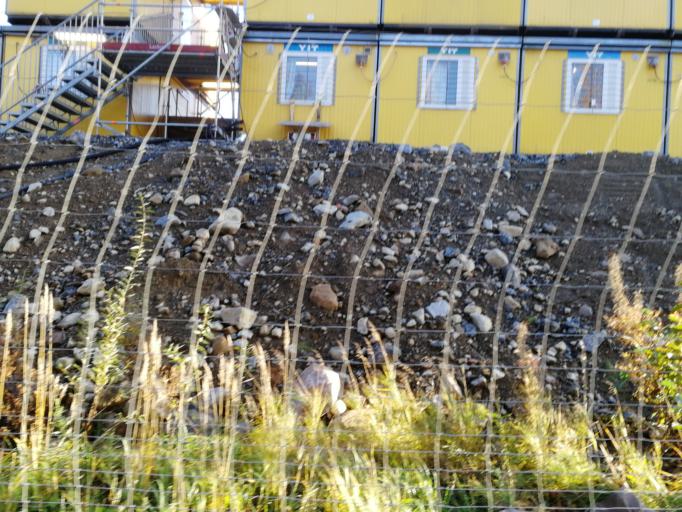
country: FI
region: Pirkanmaa
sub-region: Tampere
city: Tampere
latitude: 61.4521
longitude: 23.8730
